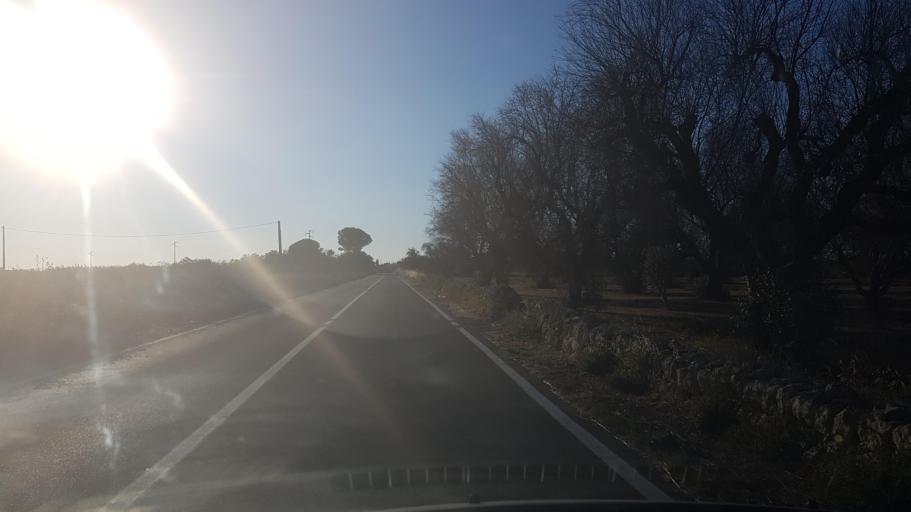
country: IT
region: Apulia
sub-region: Provincia di Lecce
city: Struda
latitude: 40.3299
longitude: 18.3015
